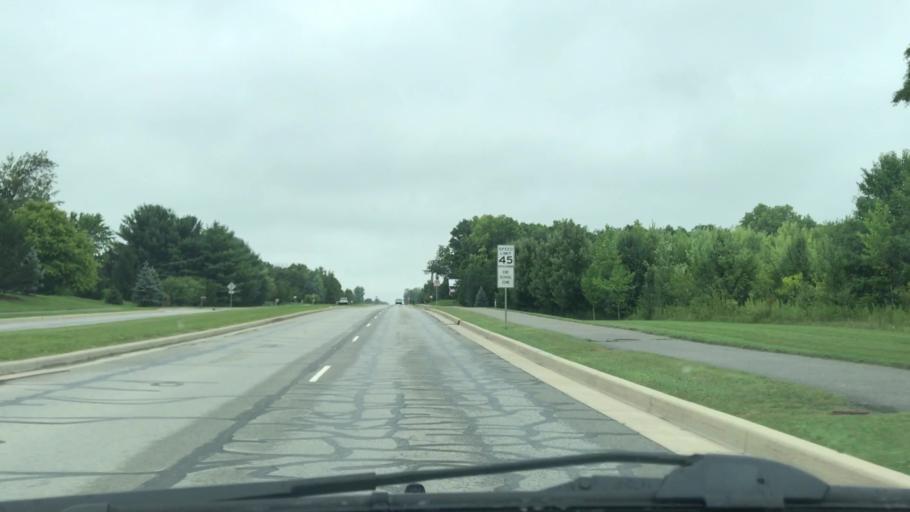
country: US
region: Indiana
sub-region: Hamilton County
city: Carmel
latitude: 40.0148
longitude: -86.0705
